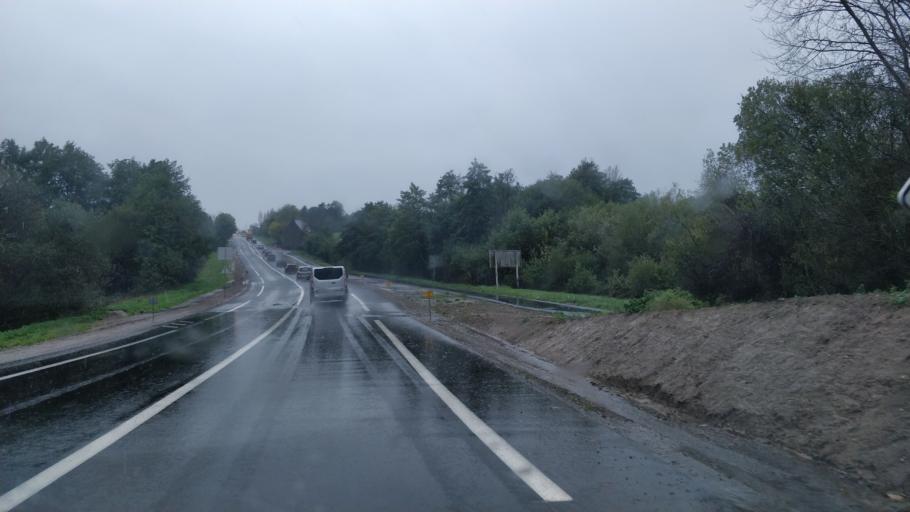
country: FR
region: Lower Normandy
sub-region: Departement de la Manche
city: Brehal
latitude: 48.8886
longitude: -1.5217
